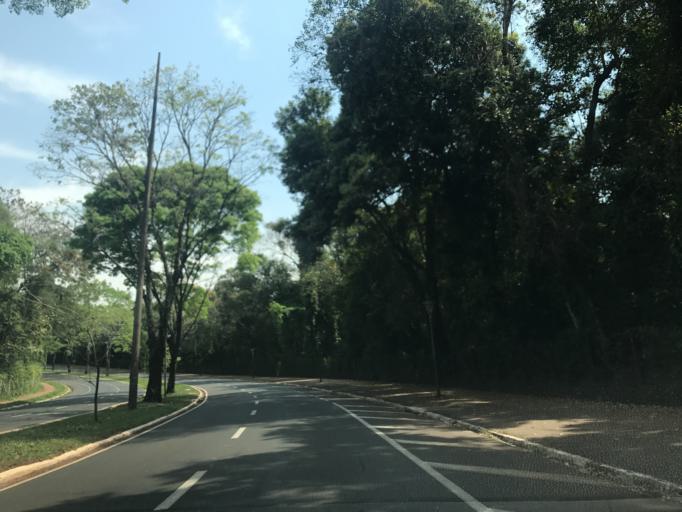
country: BR
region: Parana
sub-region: Maringa
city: Maringa
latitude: -23.4354
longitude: -51.9412
